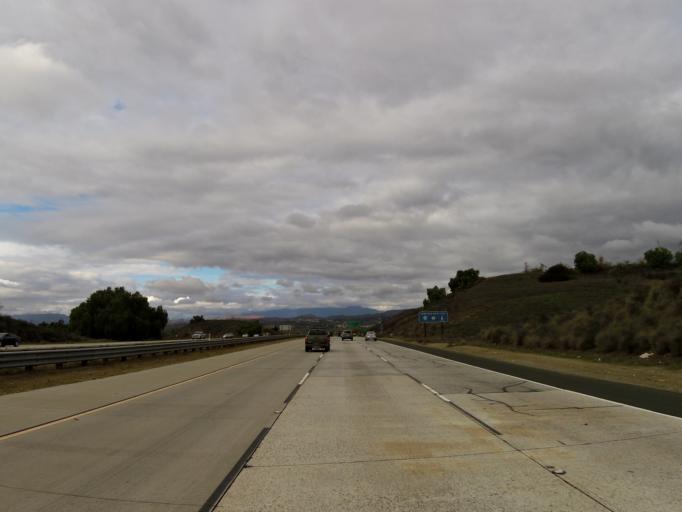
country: US
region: California
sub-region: Ventura County
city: Moorpark
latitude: 34.2726
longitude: -118.8558
